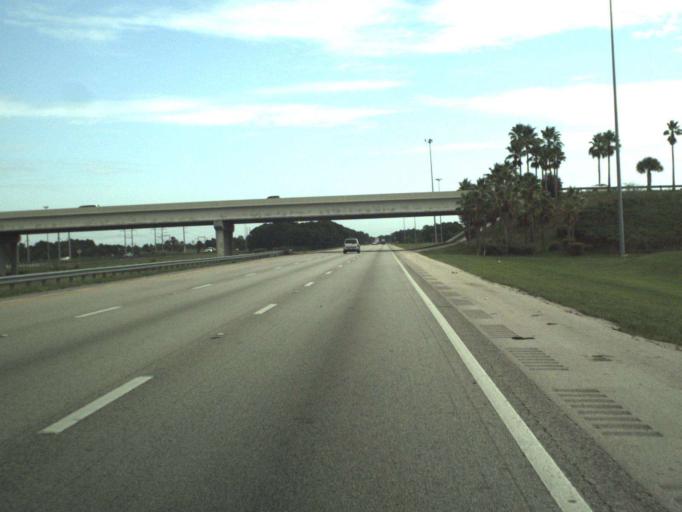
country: US
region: Florida
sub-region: Saint Lucie County
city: Port Saint Lucie
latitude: 27.3101
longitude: -80.4138
